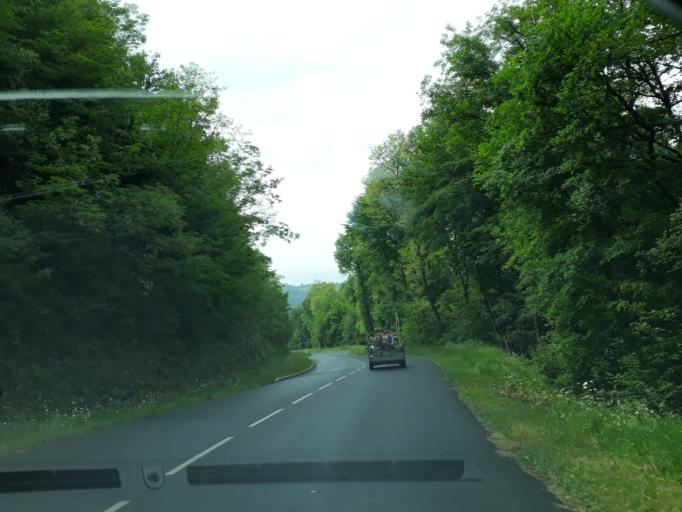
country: FR
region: Limousin
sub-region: Departement de la Correze
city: Beynat
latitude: 45.1246
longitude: 1.6893
